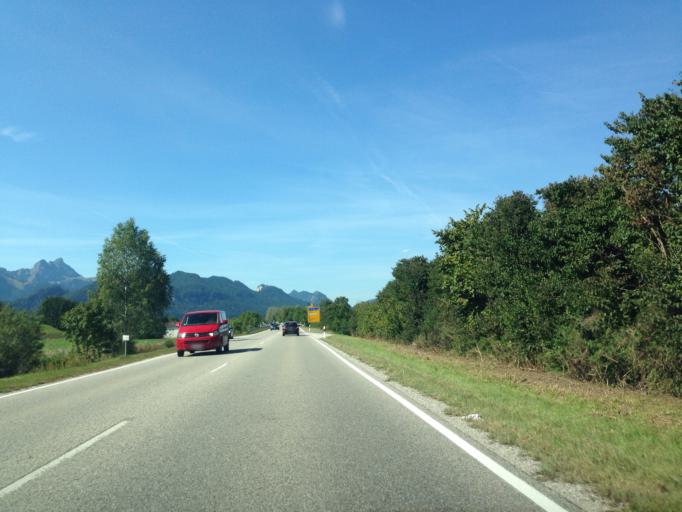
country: DE
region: Bavaria
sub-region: Swabia
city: Fuessen
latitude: 47.5804
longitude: 10.6850
